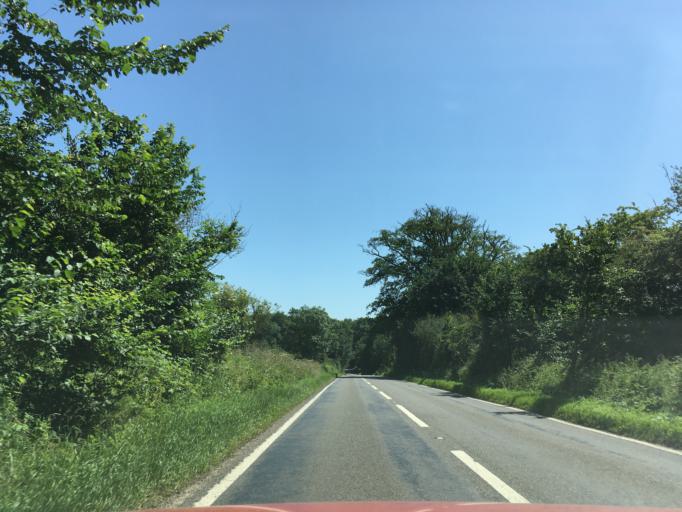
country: GB
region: England
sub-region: Oxfordshire
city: Somerton
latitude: 51.9960
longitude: -1.2285
